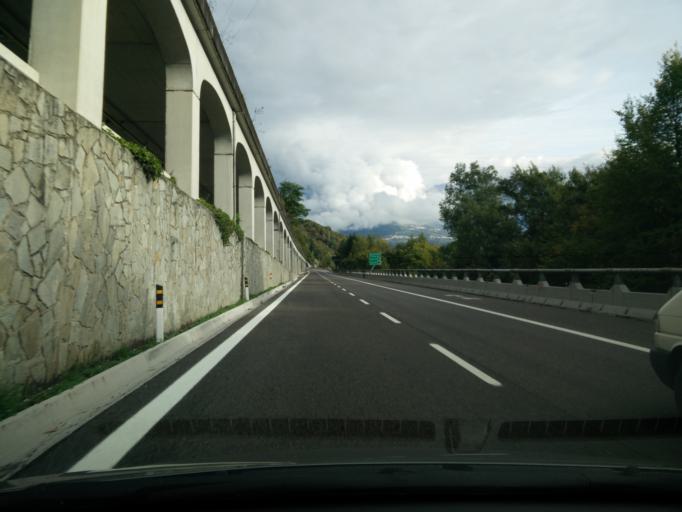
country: IT
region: Veneto
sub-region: Provincia di Belluno
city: Farra d'Alpago
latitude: 46.0964
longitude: 12.3242
